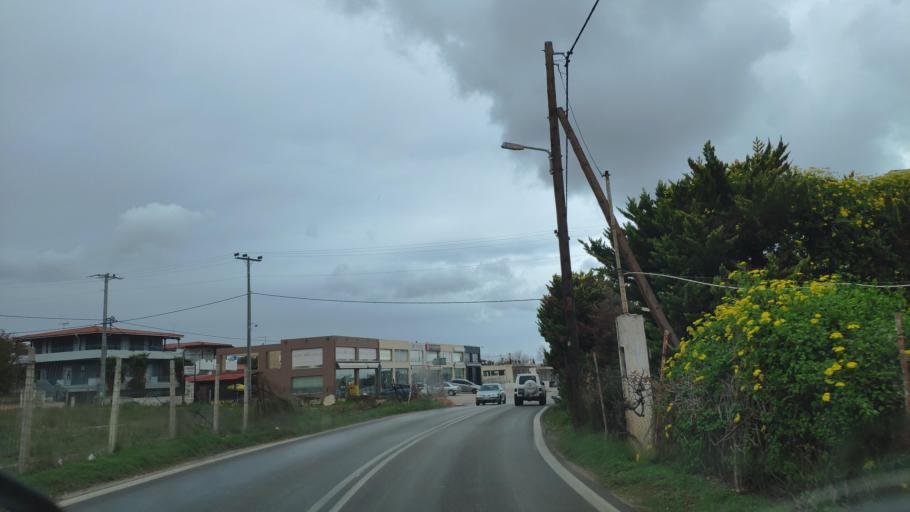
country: GR
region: Attica
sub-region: Nomarchia Anatolikis Attikis
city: Artemida
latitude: 37.9497
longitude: 24.0074
